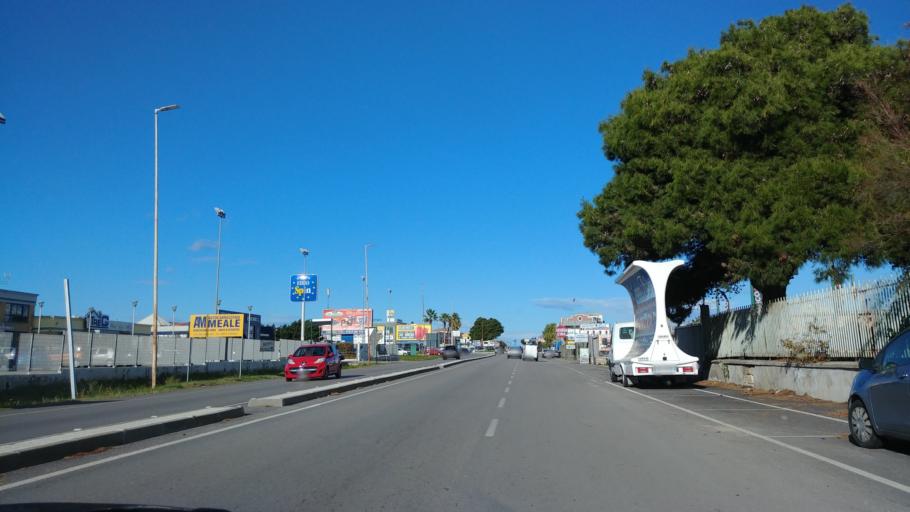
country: IT
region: Molise
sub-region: Provincia di Campobasso
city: Termoli
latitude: 41.9808
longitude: 15.0072
